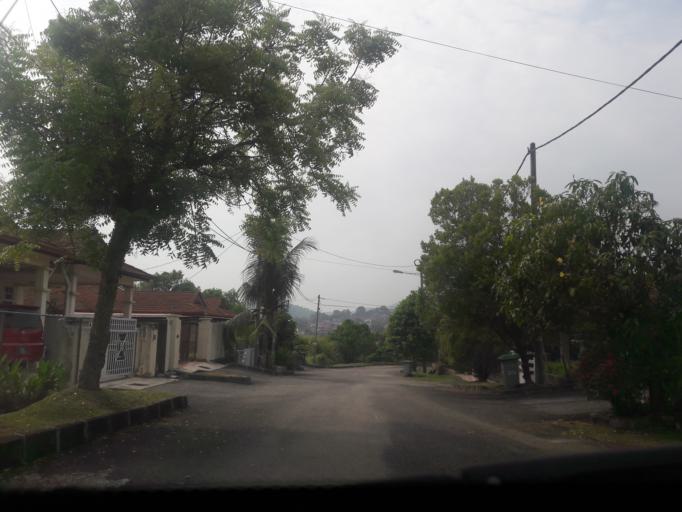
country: MY
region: Kedah
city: Kulim
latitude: 5.3587
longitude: 100.5378
